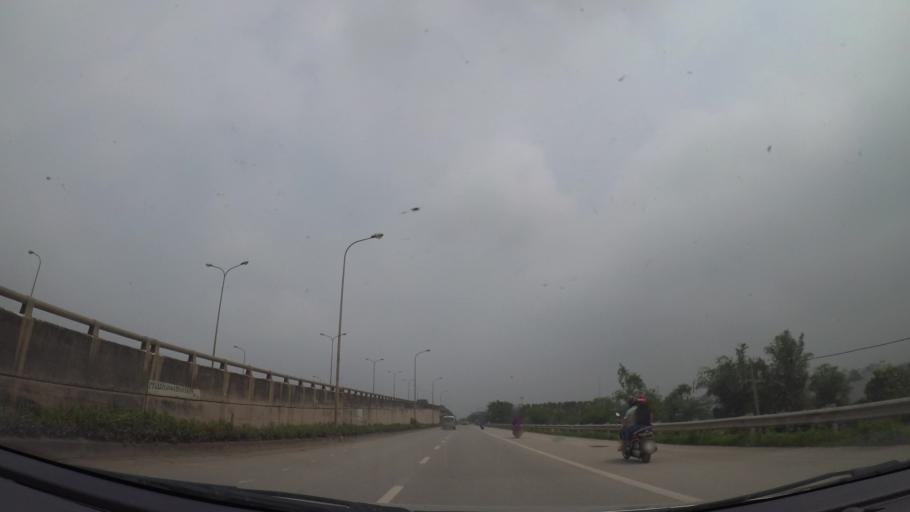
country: VN
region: Ha Noi
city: Tay Ho
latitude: 21.1231
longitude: 105.7823
